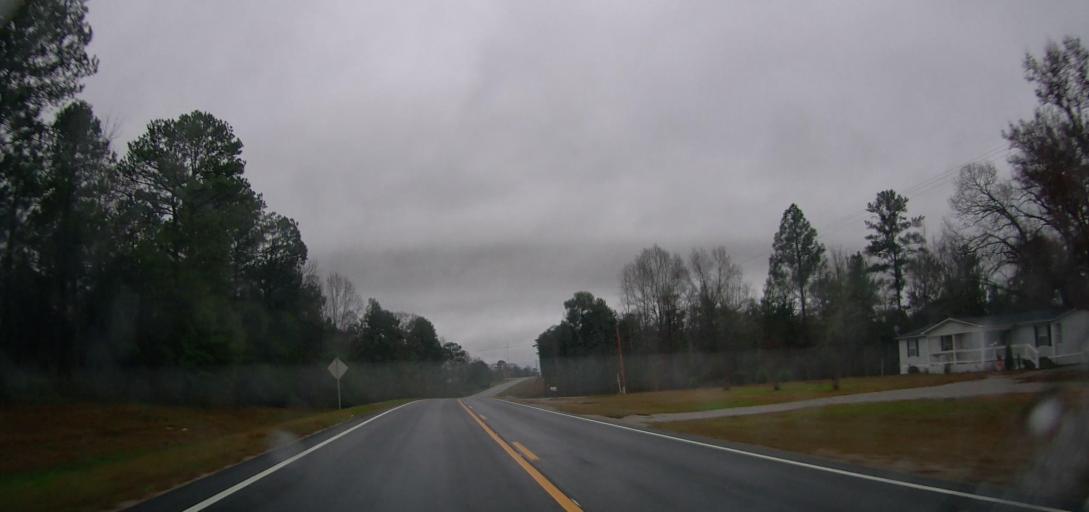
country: US
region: Alabama
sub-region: Chilton County
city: Thorsby
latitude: 32.7985
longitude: -86.9106
